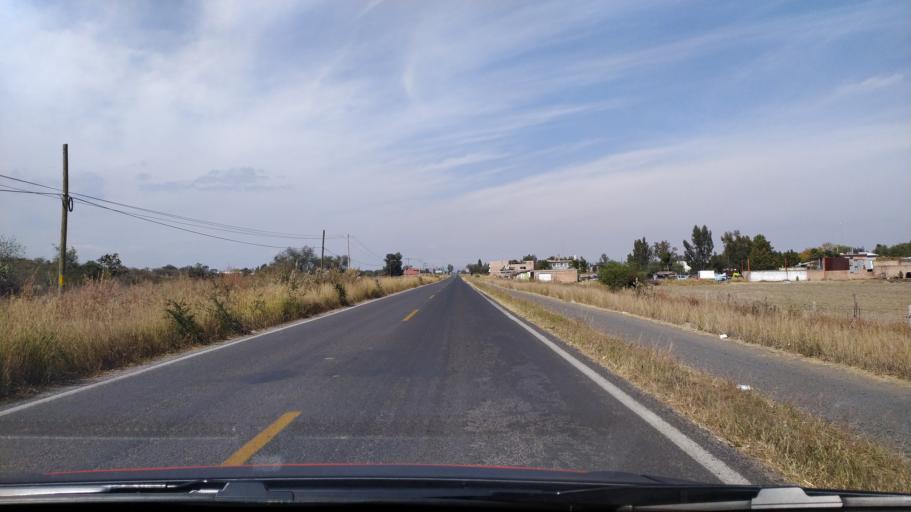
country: MX
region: Guanajuato
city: Ciudad Manuel Doblado
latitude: 20.7524
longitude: -101.9631
